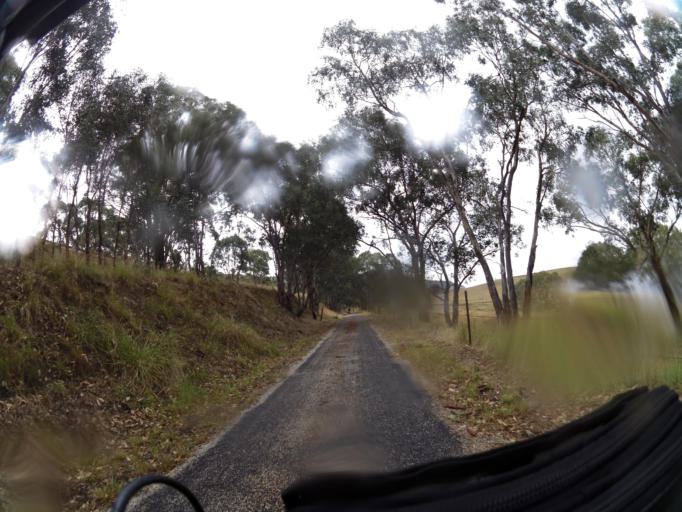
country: AU
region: New South Wales
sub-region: Albury Municipality
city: East Albury
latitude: -36.2154
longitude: 147.2380
